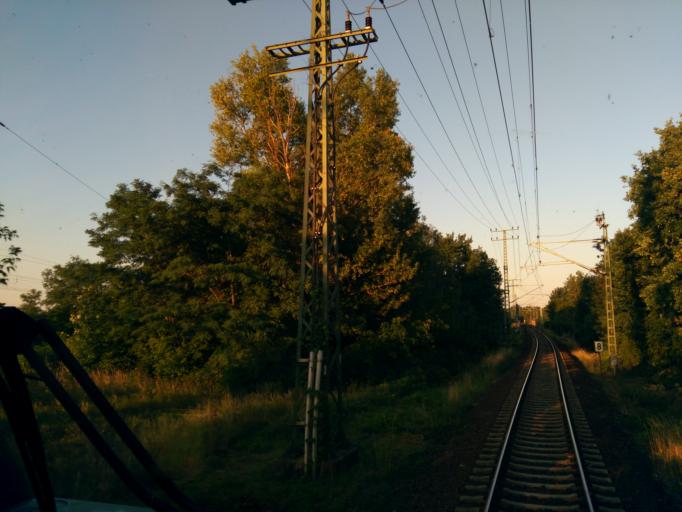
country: DE
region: Berlin
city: Adlershof
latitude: 52.4253
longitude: 13.5610
